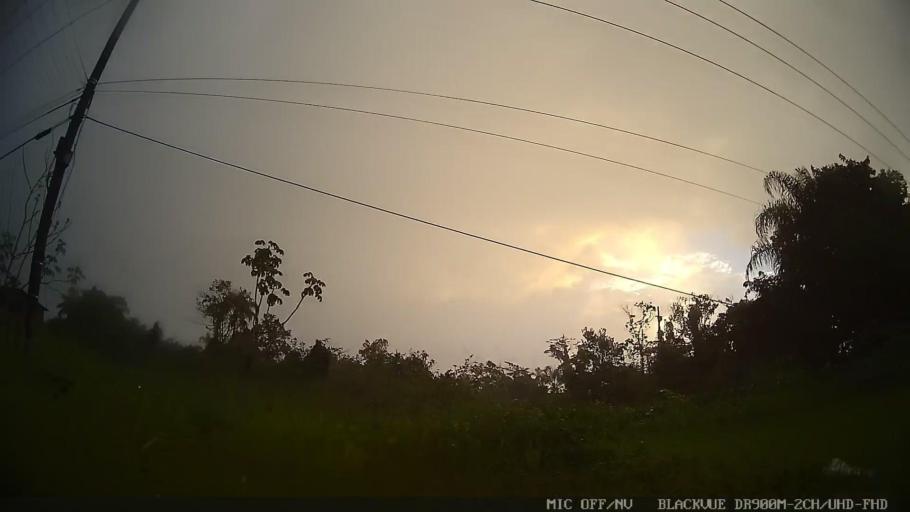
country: BR
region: Sao Paulo
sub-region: Itanhaem
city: Itanhaem
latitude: -24.1237
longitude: -46.7826
